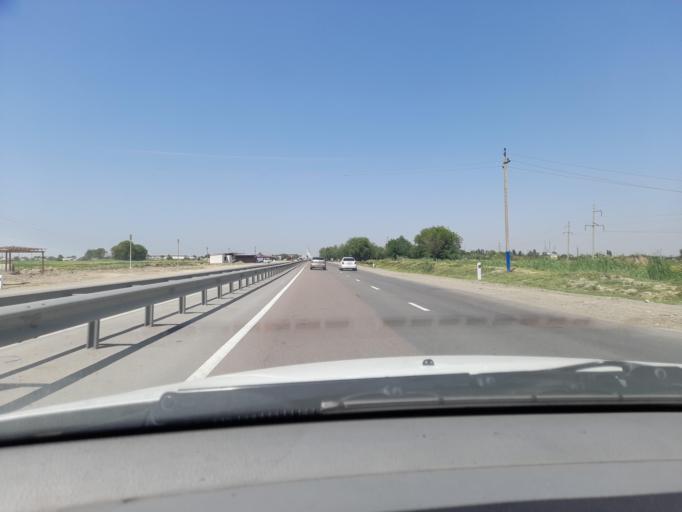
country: KZ
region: Ongtustik Qazaqstan
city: Myrzakent
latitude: 40.5351
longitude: 68.4289
